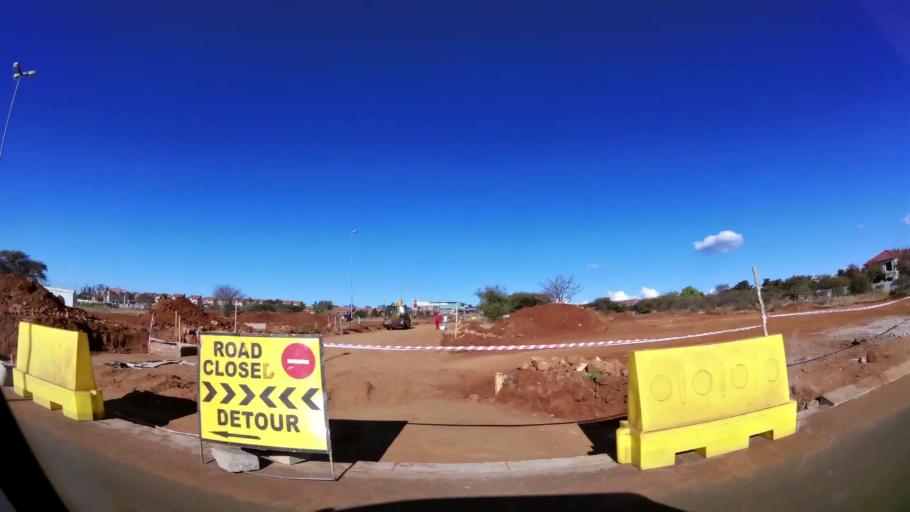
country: ZA
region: Limpopo
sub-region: Capricorn District Municipality
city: Polokwane
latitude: -23.8830
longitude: 29.4946
